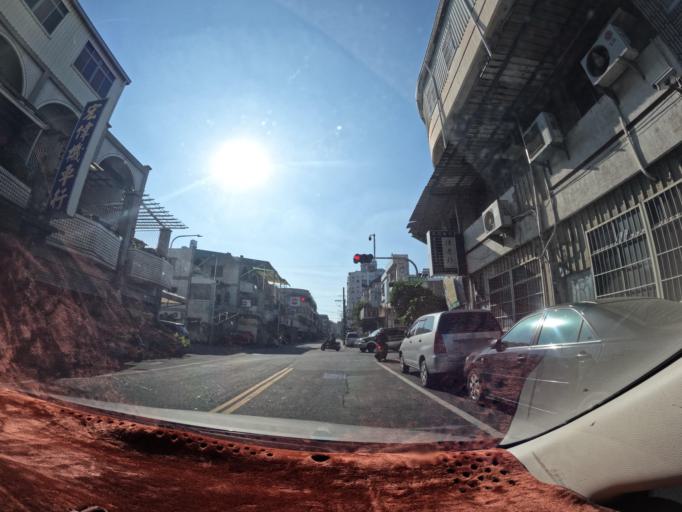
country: TW
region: Taiwan
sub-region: Tainan
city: Tainan
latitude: 23.0334
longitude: 120.2523
